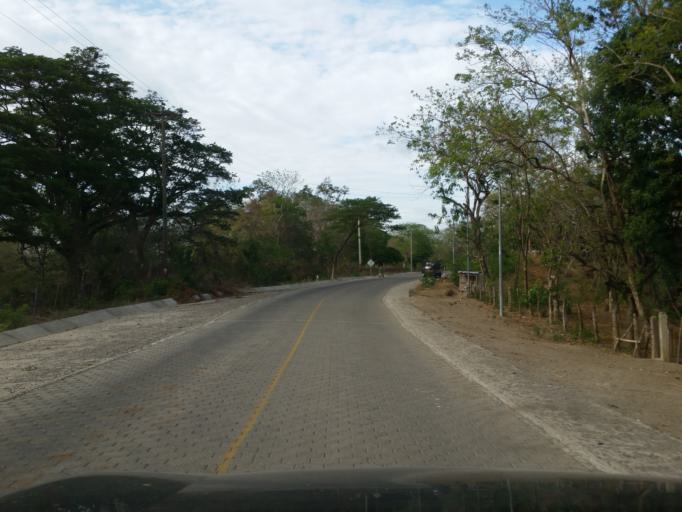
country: NI
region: Rivas
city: Tola
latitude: 11.4011
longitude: -85.9575
